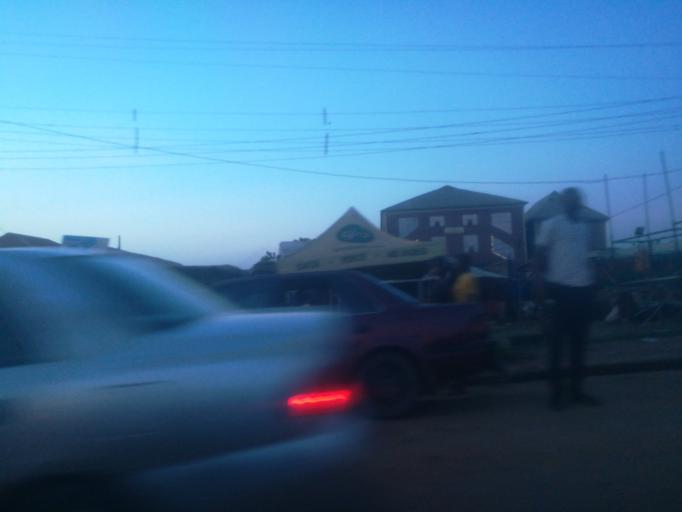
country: NG
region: Ogun
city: Abeokuta
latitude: 7.1874
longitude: 3.4357
